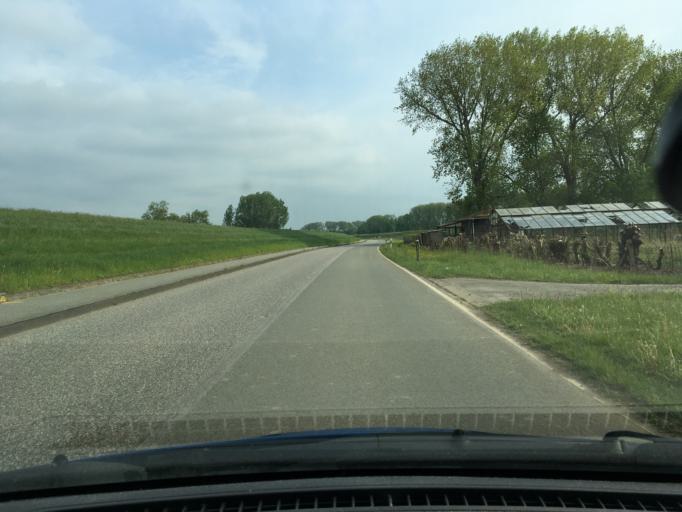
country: DE
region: Hamburg
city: Rothenburgsort
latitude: 53.4886
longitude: 10.0487
